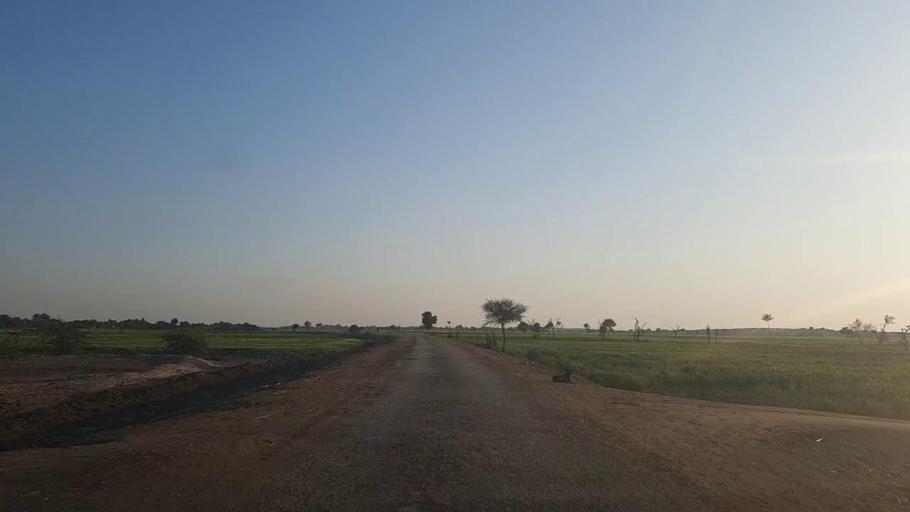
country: PK
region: Sindh
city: Jam Sahib
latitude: 26.3380
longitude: 68.6956
